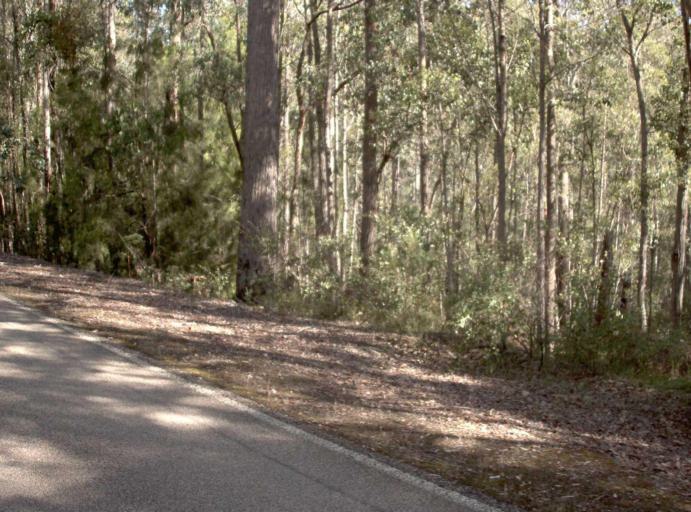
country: AU
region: Victoria
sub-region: East Gippsland
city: Lakes Entrance
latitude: -37.5624
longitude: 148.5571
